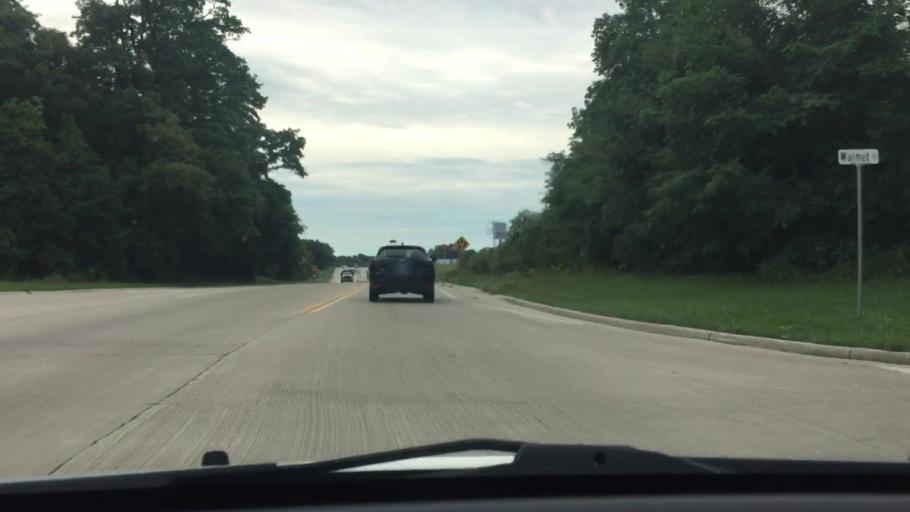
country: US
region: Wisconsin
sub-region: Waukesha County
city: North Prairie
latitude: 42.9521
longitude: -88.3560
